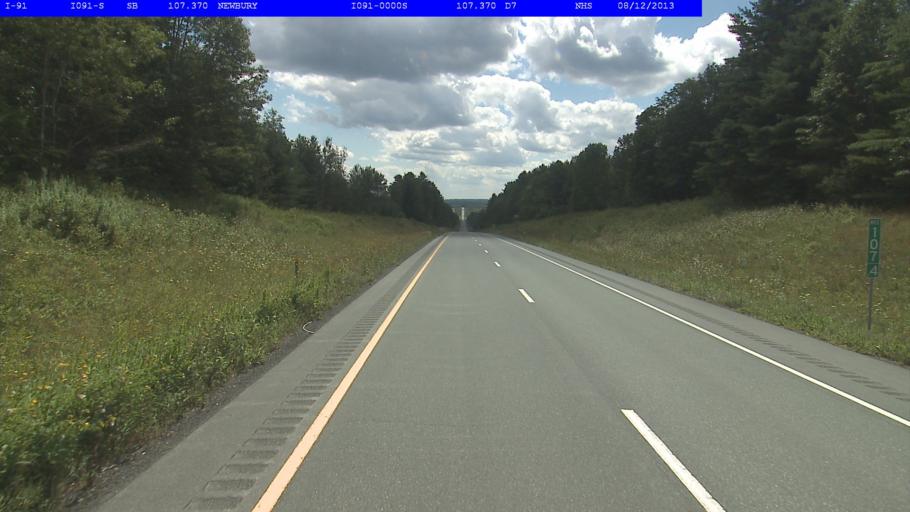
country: US
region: New Hampshire
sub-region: Grafton County
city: Woodsville
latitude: 44.1198
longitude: -72.1057
